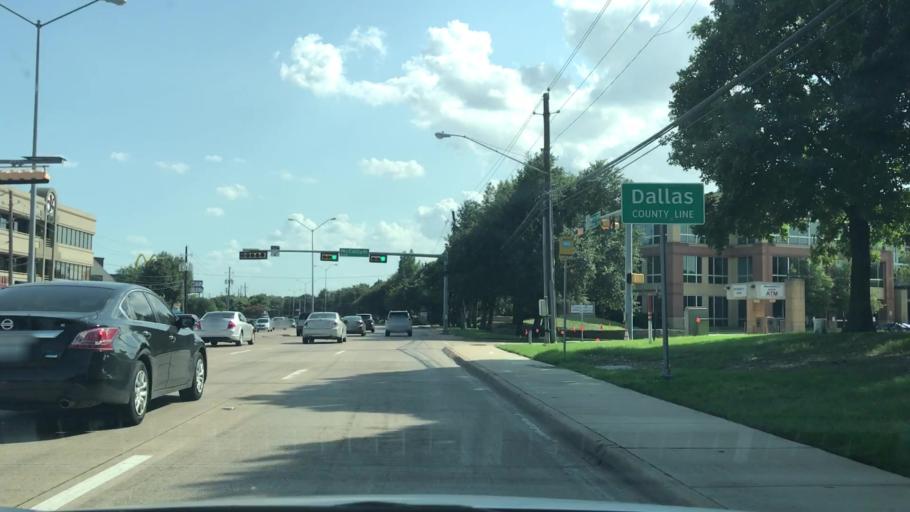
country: US
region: Texas
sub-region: Dallas County
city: Addison
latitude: 32.9872
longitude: -96.8033
